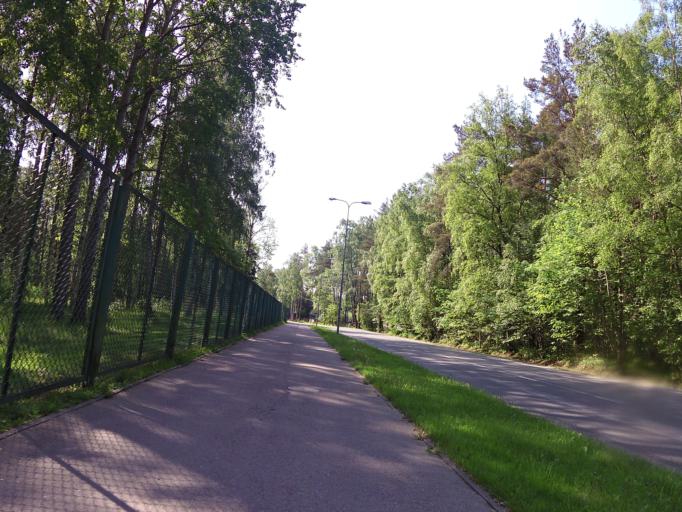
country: EE
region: Harju
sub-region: Saue vald
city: Laagri
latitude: 59.4358
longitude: 24.6281
